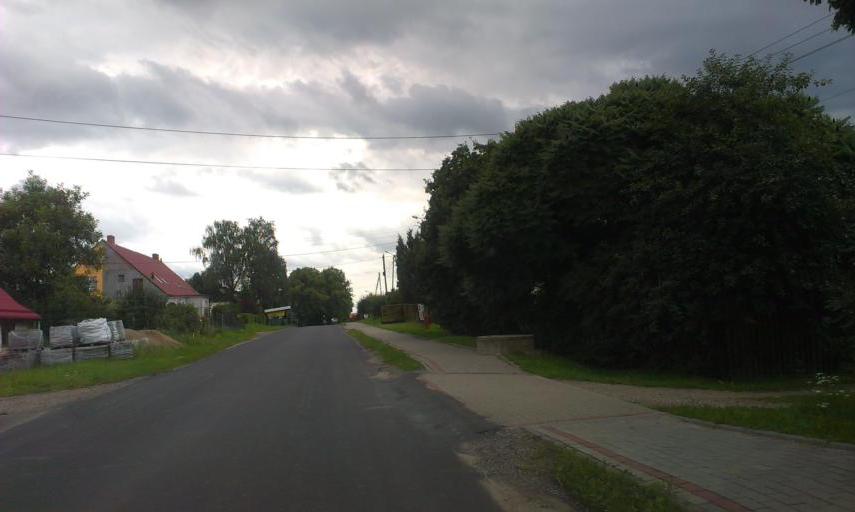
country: PL
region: West Pomeranian Voivodeship
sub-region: Powiat bialogardzki
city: Tychowo
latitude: 53.9370
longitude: 16.2390
